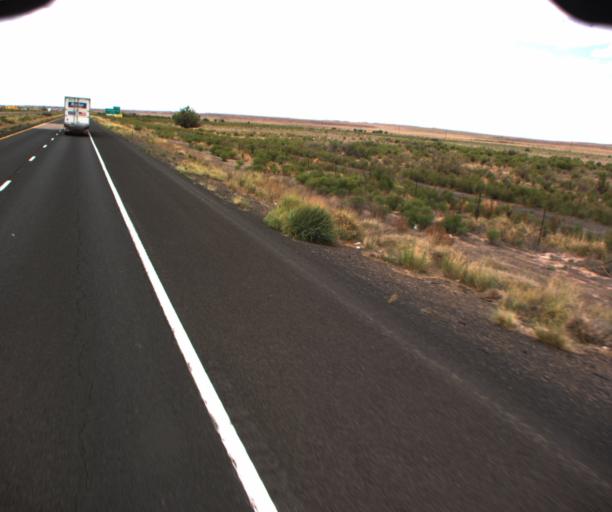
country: US
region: Arizona
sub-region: Navajo County
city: Joseph City
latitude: 34.9668
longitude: -110.4169
